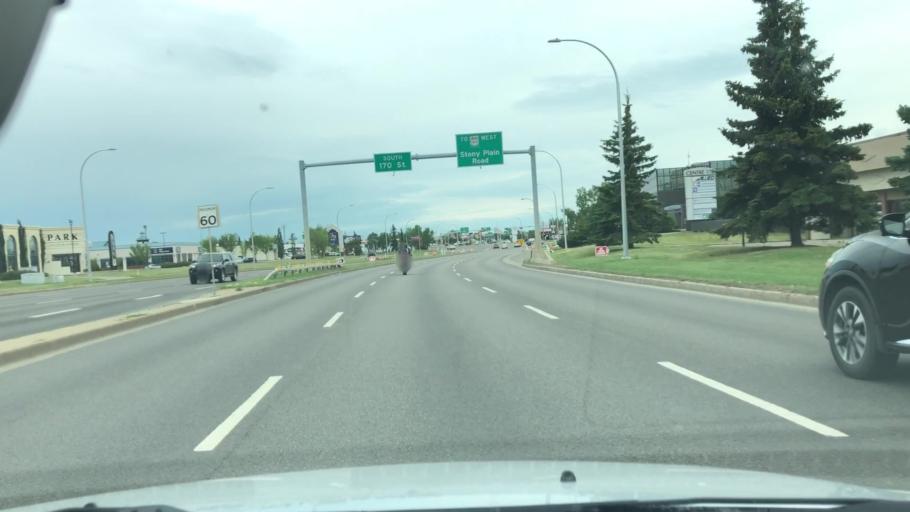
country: CA
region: Alberta
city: St. Albert
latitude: 53.5480
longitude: -113.6154
